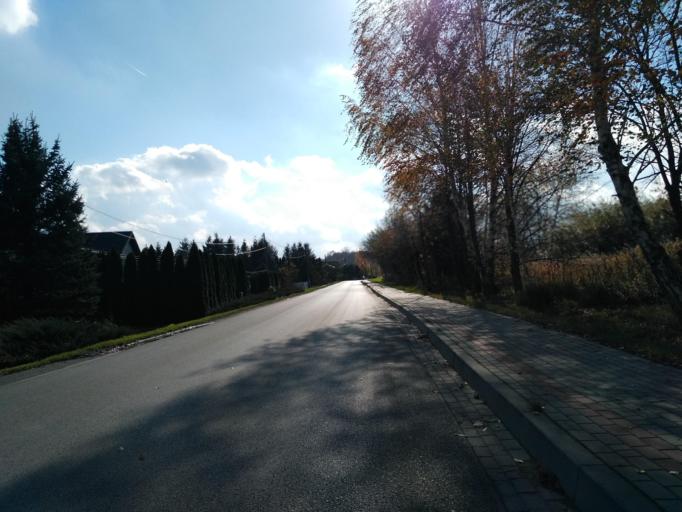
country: PL
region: Subcarpathian Voivodeship
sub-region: Powiat rzeszowski
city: Trzciana
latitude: 50.0823
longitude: 21.8398
